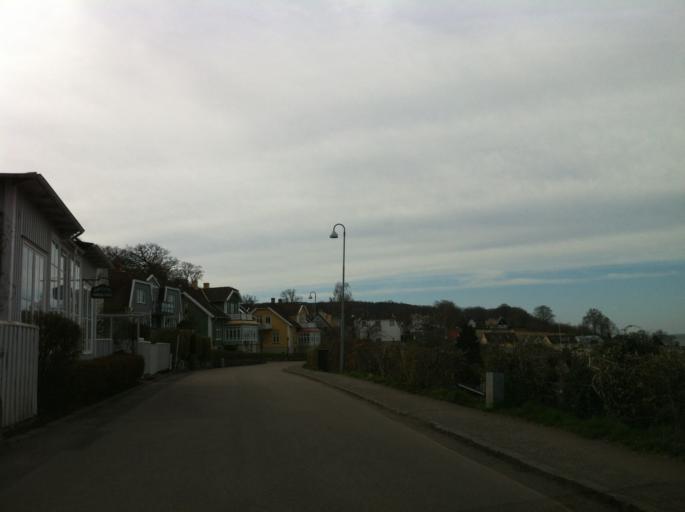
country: SE
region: Skane
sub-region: Hoganas Kommun
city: Hoganas
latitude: 56.2736
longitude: 12.5744
